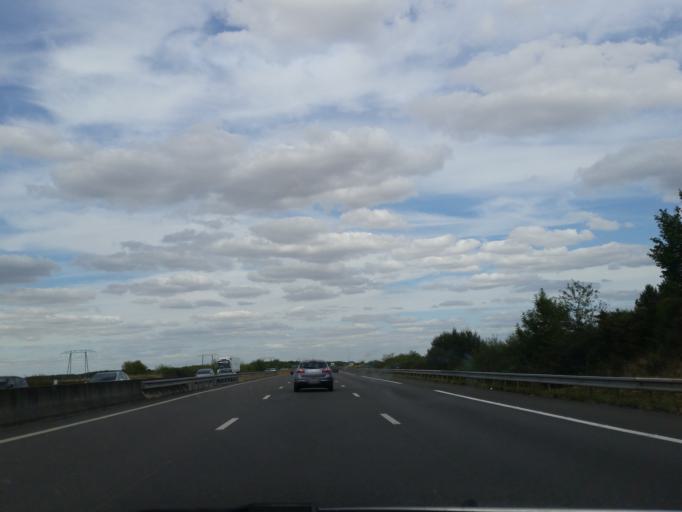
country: FR
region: Centre
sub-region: Departement du Loir-et-Cher
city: Herbault
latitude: 47.5973
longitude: 1.1005
